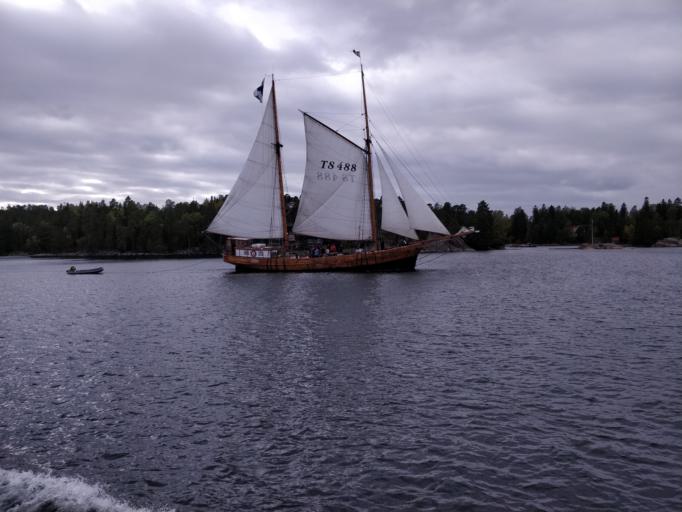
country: FI
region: Uusimaa
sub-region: Helsinki
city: Vantaa
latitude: 60.1700
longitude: 25.0953
